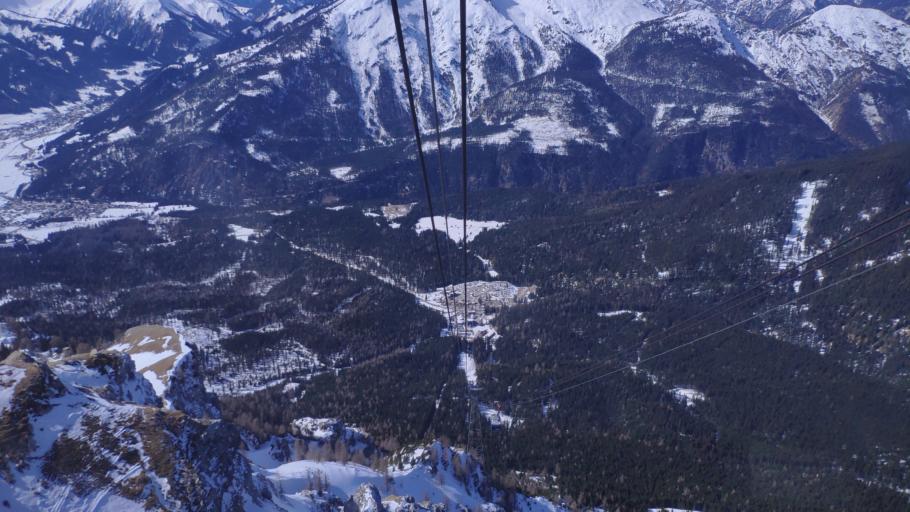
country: AT
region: Tyrol
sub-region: Politischer Bezirk Reutte
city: Ehrwald
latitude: 47.4238
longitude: 10.9651
